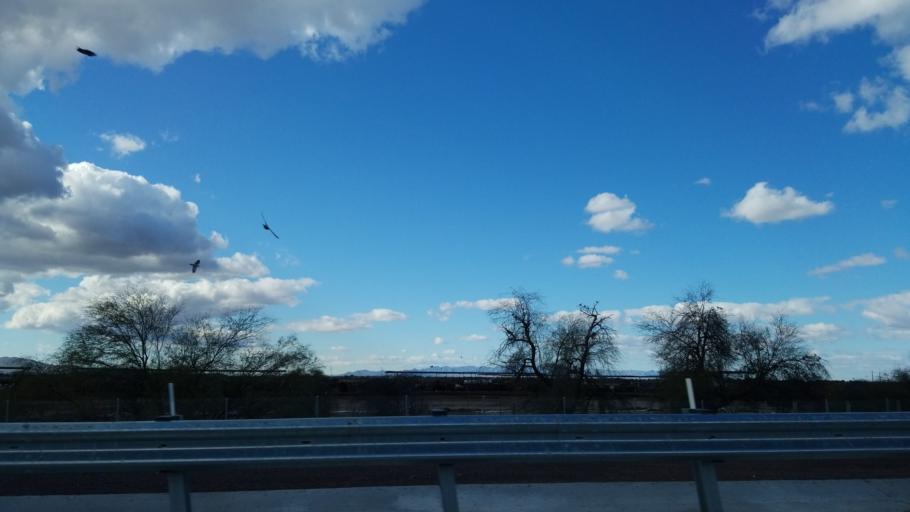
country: US
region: Arizona
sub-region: Maricopa County
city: Laveen
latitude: 33.3648
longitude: -112.1919
